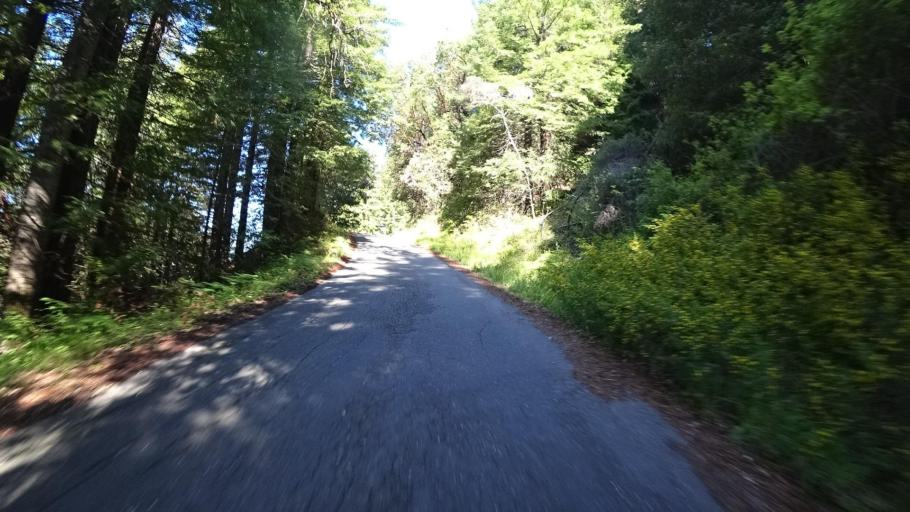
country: US
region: California
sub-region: Humboldt County
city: Rio Dell
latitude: 40.4556
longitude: -123.9936
